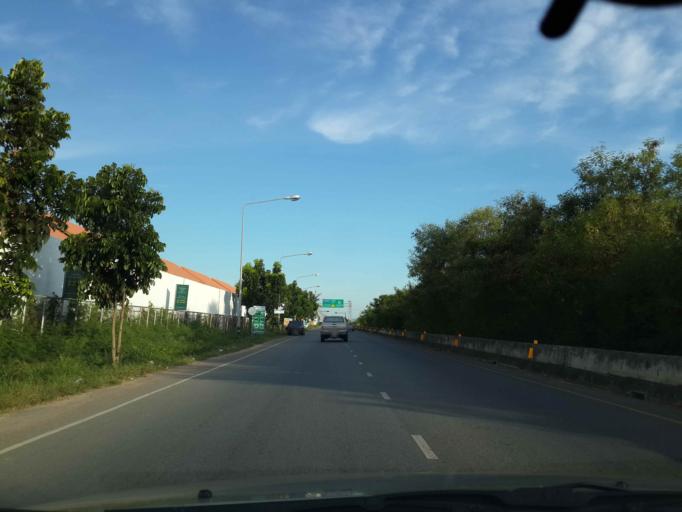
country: TH
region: Chon Buri
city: Phatthaya
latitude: 12.8806
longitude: 100.9053
